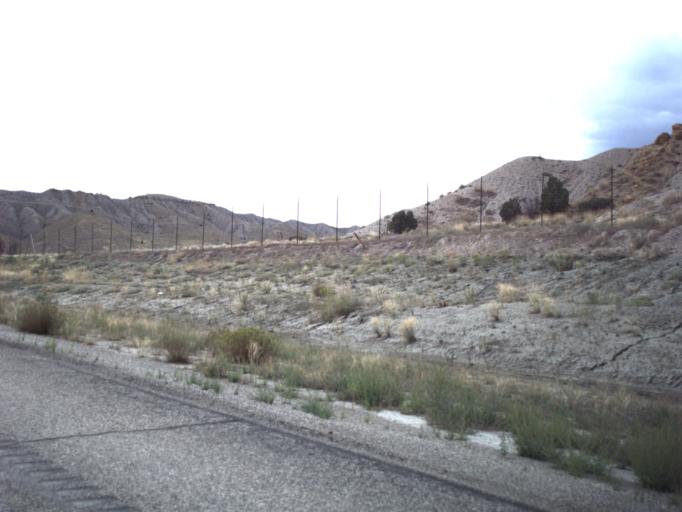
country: US
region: Utah
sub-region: Carbon County
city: Carbonville
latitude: 39.6286
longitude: -110.8616
